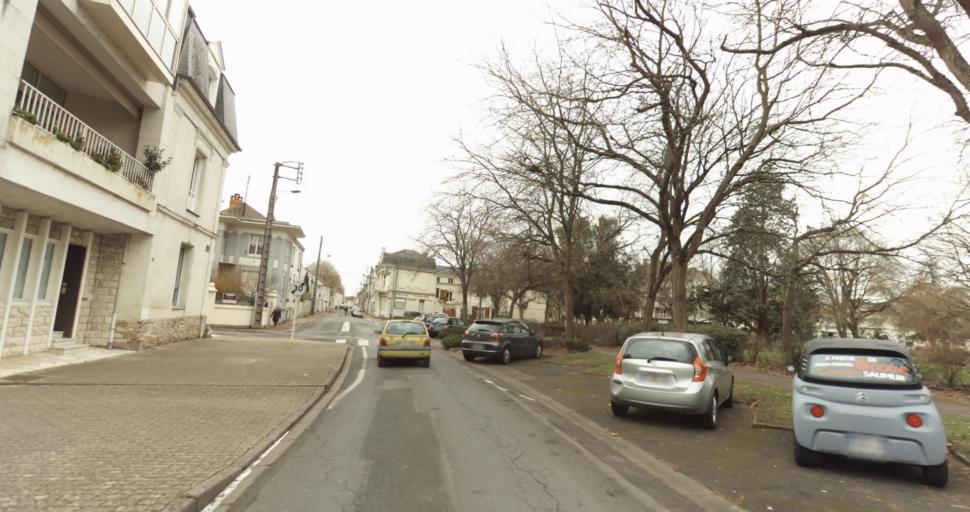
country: FR
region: Pays de la Loire
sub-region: Departement de Maine-et-Loire
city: Saumur
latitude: 47.2555
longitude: -0.0804
